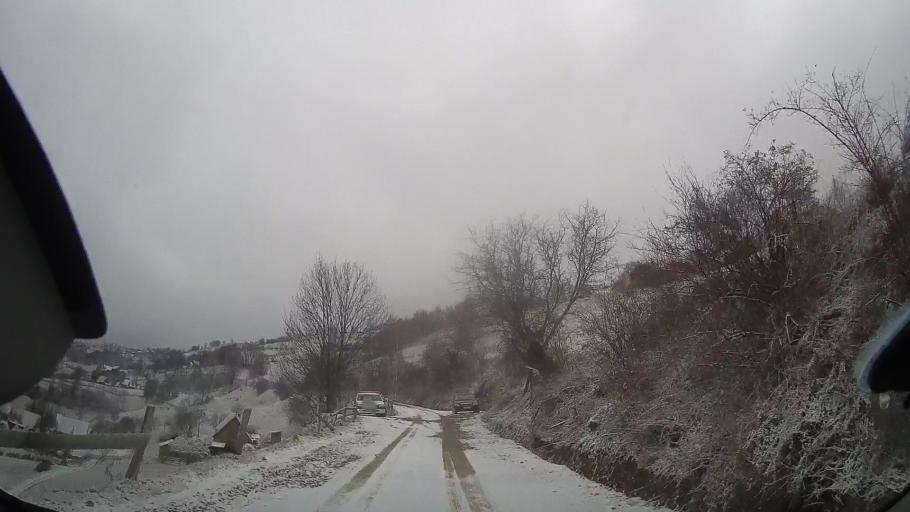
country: RO
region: Cluj
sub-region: Comuna Maguri-Racatau
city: Maguri-Racatau
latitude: 46.6614
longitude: 23.1912
